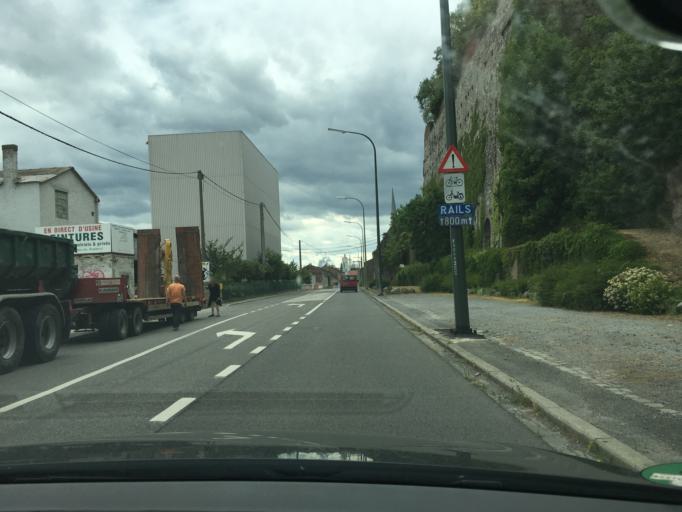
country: BE
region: Wallonia
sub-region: Province de Liege
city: Engis
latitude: 50.5703
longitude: 5.3747
